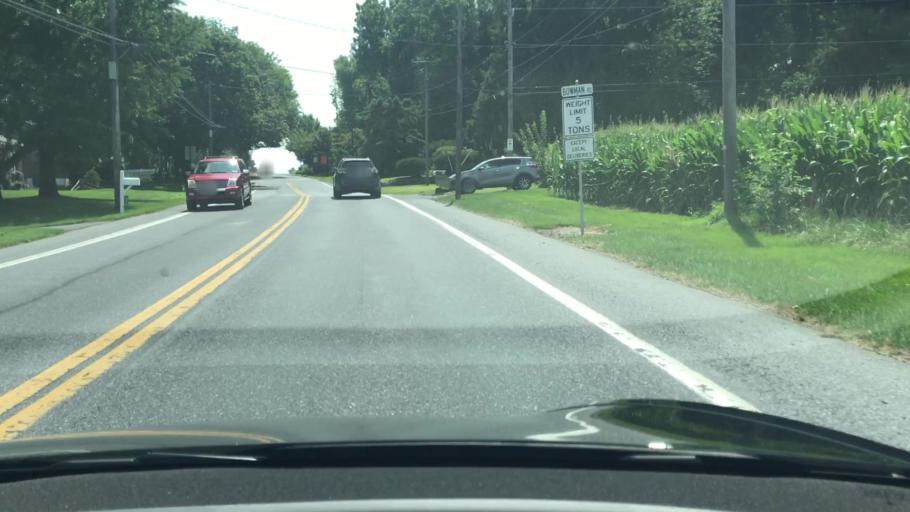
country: US
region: Pennsylvania
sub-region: Lancaster County
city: Landisville
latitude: 40.0817
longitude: -76.4086
